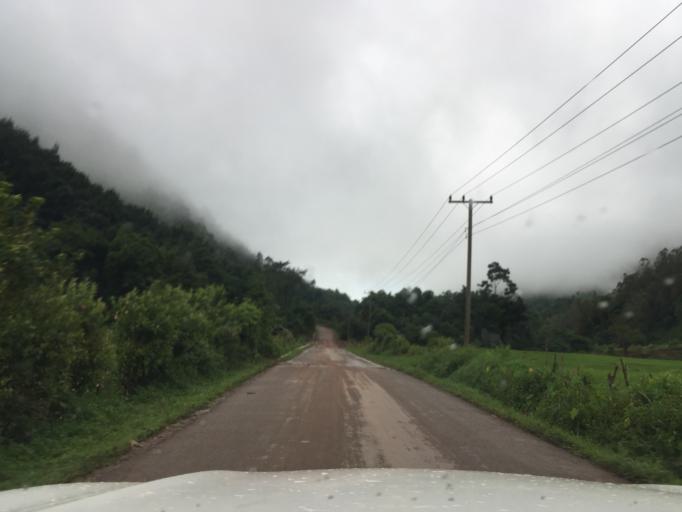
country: LA
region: Oudomxai
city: Muang La
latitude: 20.8309
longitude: 102.0987
